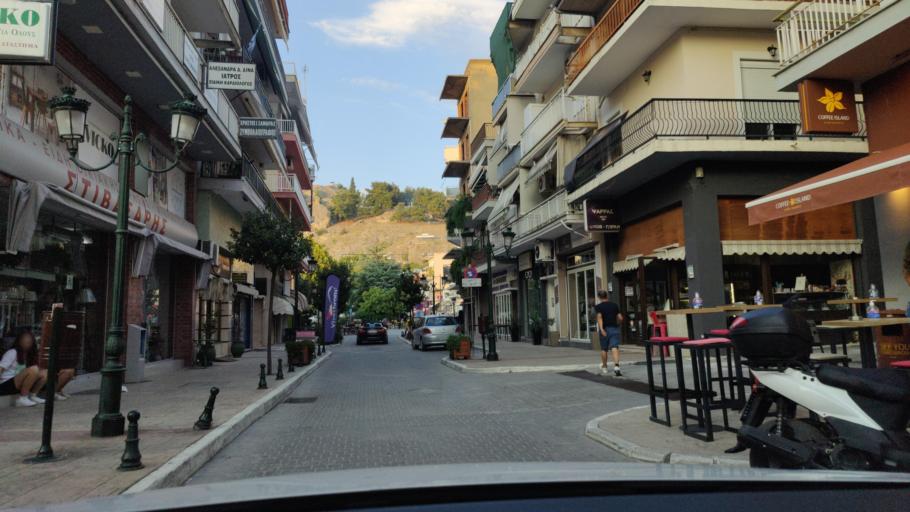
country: GR
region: Central Macedonia
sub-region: Nomos Serron
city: Sidirokastro
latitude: 41.2366
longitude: 23.3921
